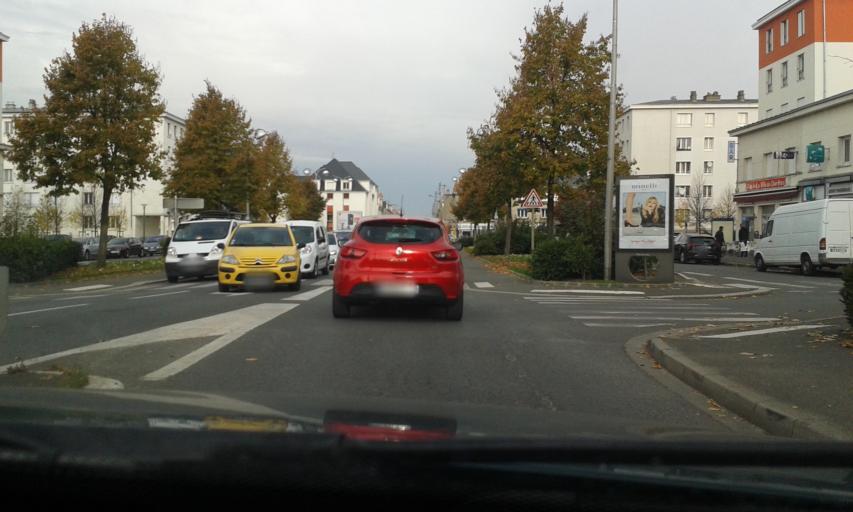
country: FR
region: Centre
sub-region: Departement du Loiret
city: Orleans
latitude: 47.9179
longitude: 1.8987
